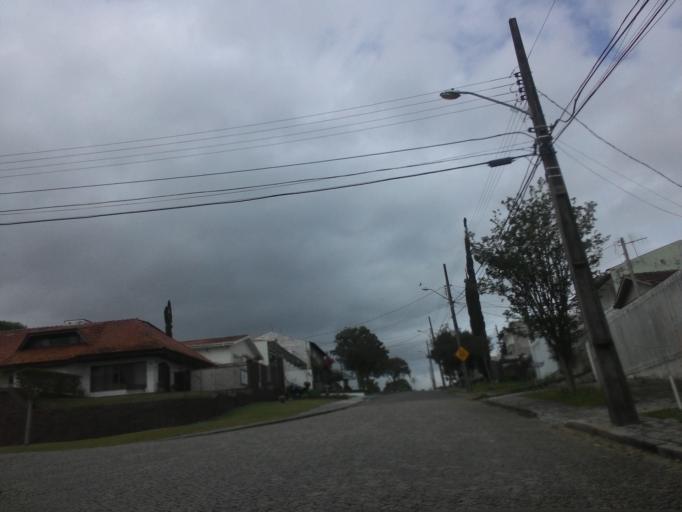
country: BR
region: Parana
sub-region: Curitiba
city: Curitiba
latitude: -25.4606
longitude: -49.2430
